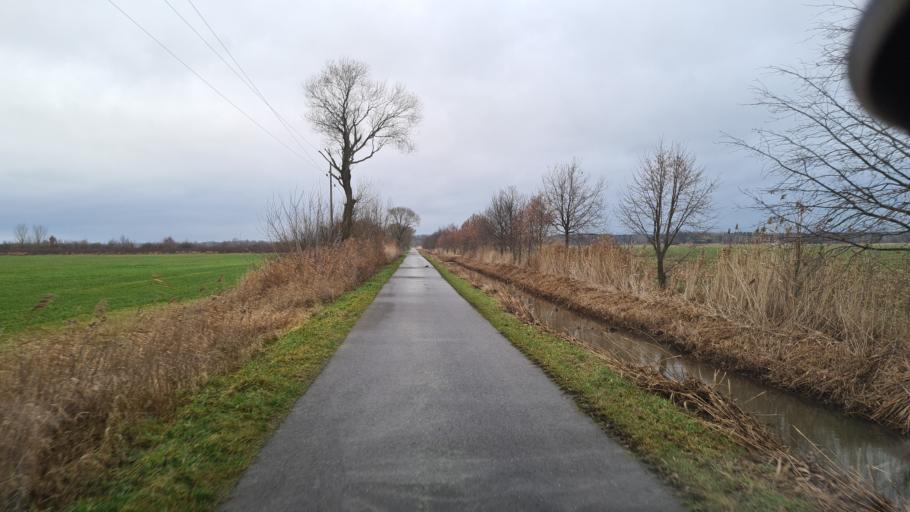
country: DE
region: Brandenburg
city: Ziltendorf
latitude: 52.2396
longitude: 14.6627
